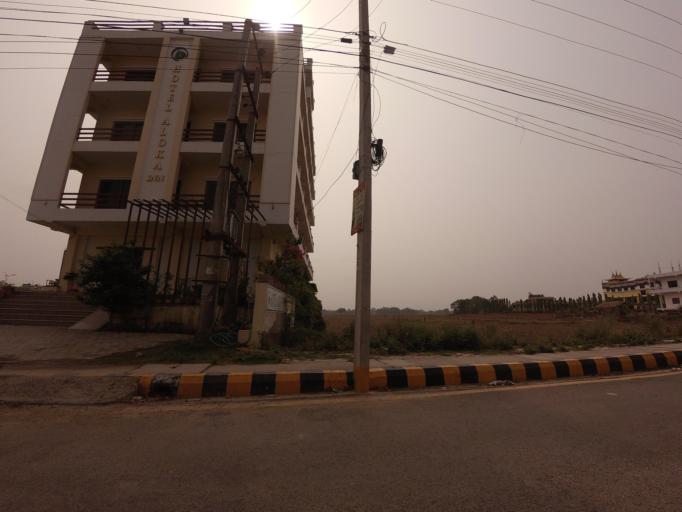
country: IN
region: Uttar Pradesh
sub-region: Maharajganj
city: Nautanwa
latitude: 27.4671
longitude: 83.2838
